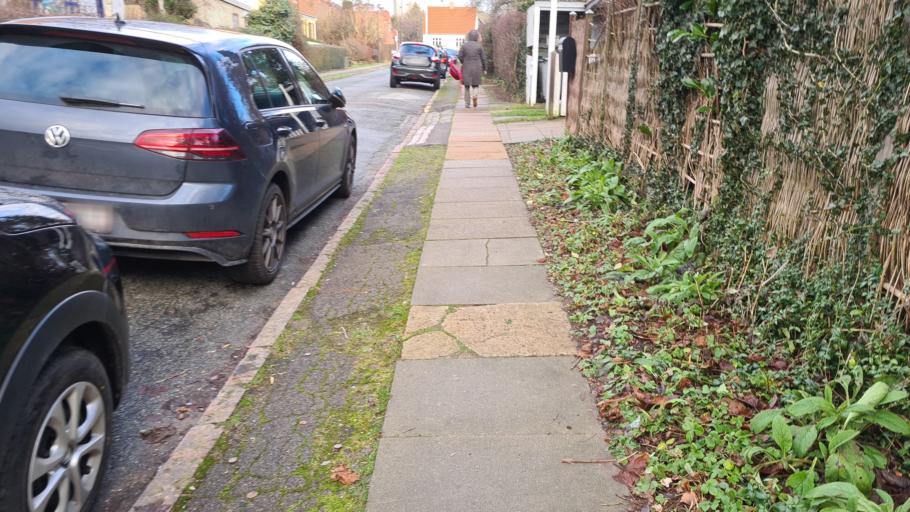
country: DK
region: Capital Region
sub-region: Kobenhavn
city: Vanlose
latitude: 55.6971
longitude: 12.5000
